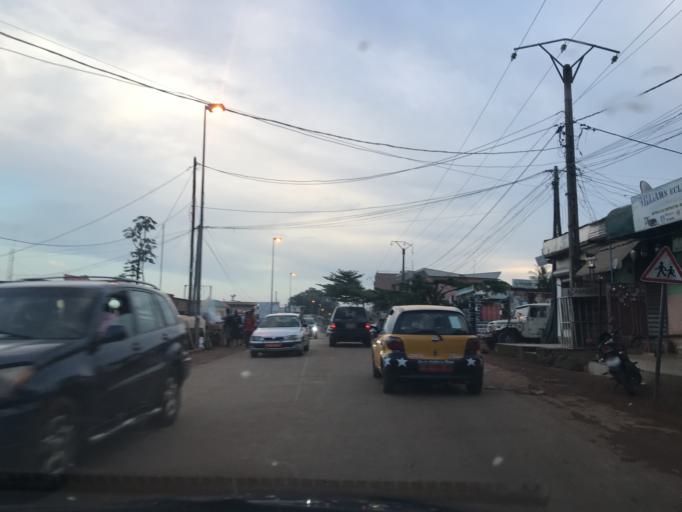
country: CM
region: Centre
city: Yaounde
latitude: 3.8813
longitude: 11.5237
